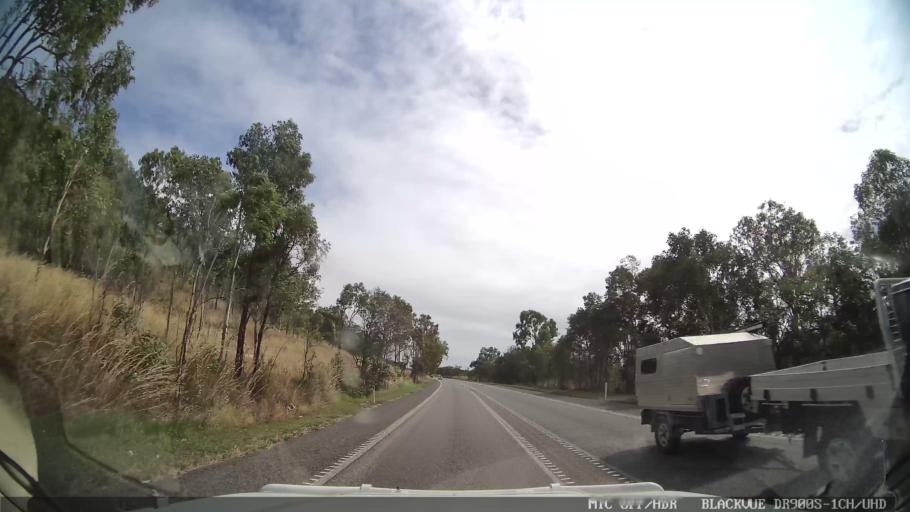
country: AU
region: Queensland
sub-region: Hinchinbrook
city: Ingham
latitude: -19.0089
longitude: 146.3625
